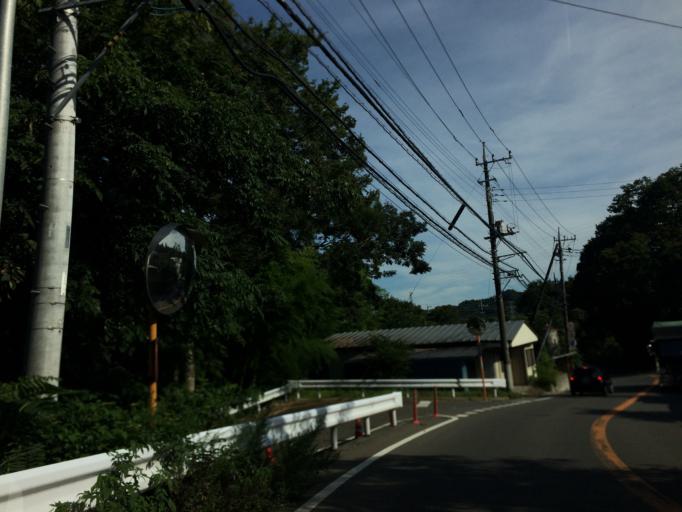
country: JP
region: Gunma
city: Shibukawa
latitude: 36.5330
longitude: 138.9682
